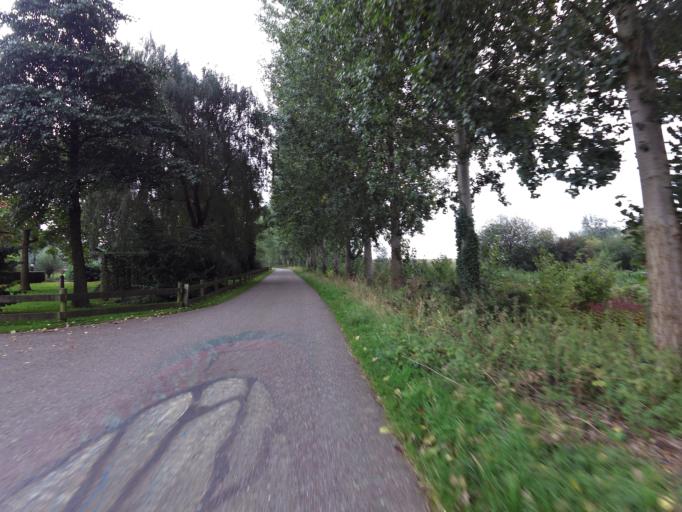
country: NL
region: Gelderland
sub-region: Gemeente Zevenaar
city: Zevenaar
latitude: 51.9085
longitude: 6.0976
